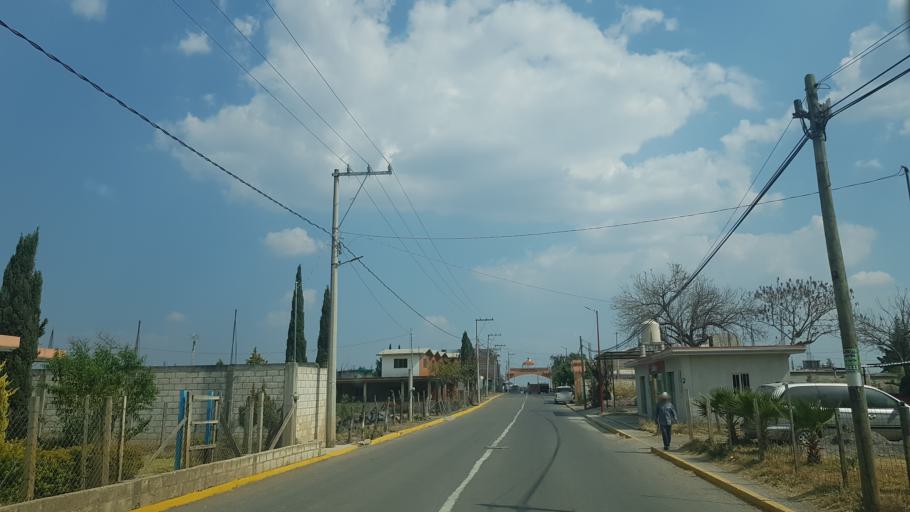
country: MX
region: Puebla
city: San Juan Amecac
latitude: 18.8287
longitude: -98.6571
